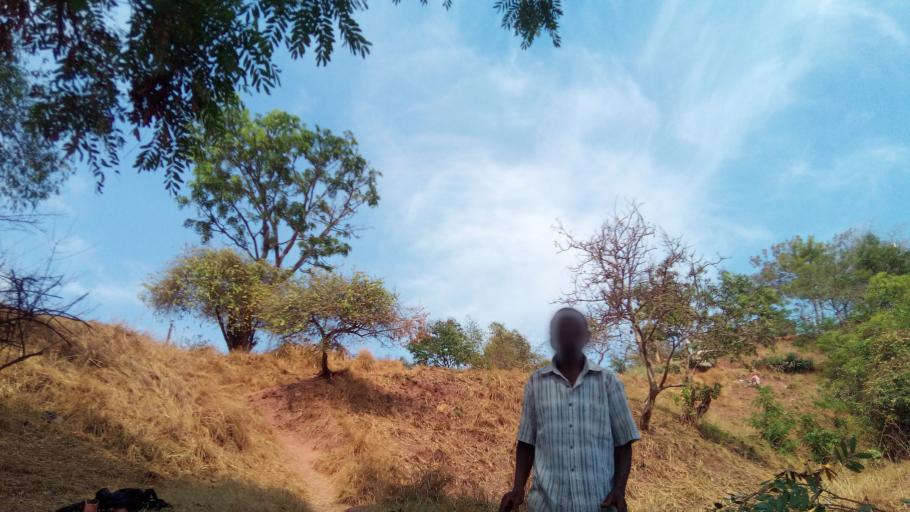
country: CD
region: Katanga
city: Kalemie
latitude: -5.9299
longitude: 29.1915
